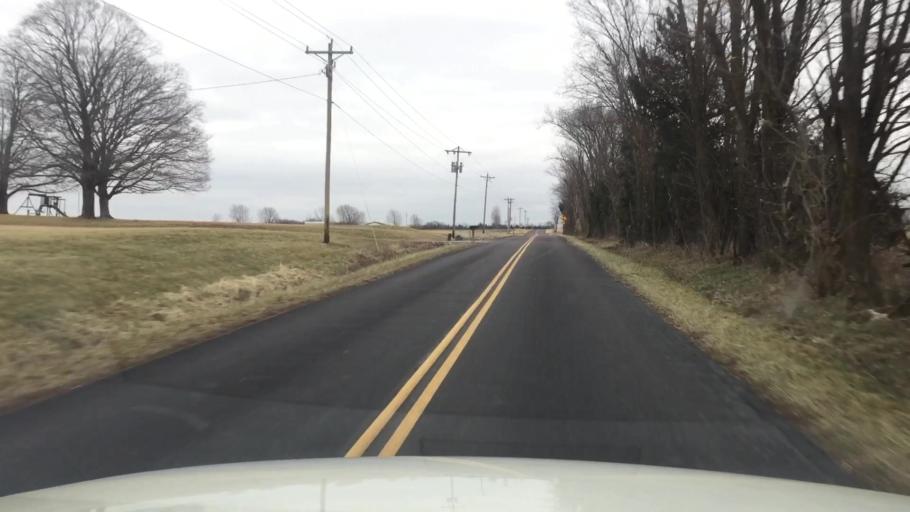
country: US
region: Missouri
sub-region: Boone County
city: Ashland
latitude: 38.8149
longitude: -92.2865
